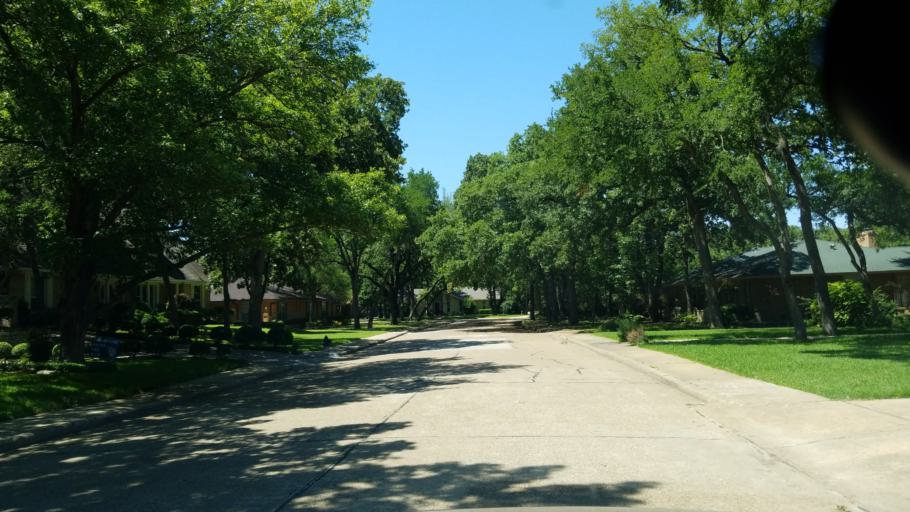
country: US
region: Texas
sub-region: Dallas County
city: Irving
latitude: 32.8309
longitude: -96.9655
